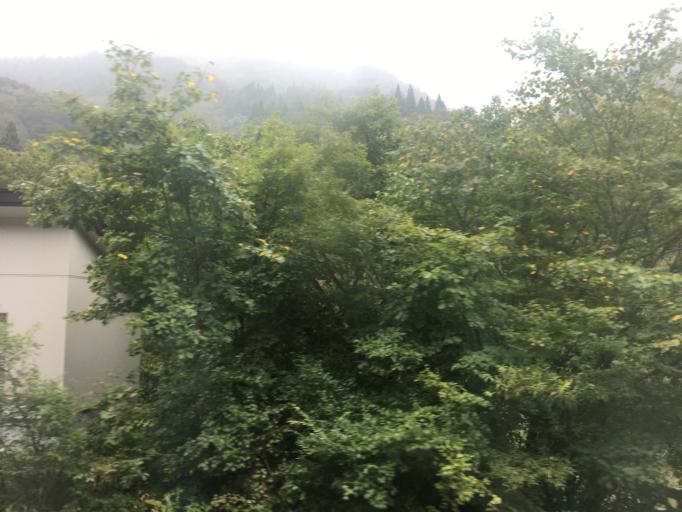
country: JP
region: Iwate
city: Shizukuishi
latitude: 39.6909
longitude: 140.7797
